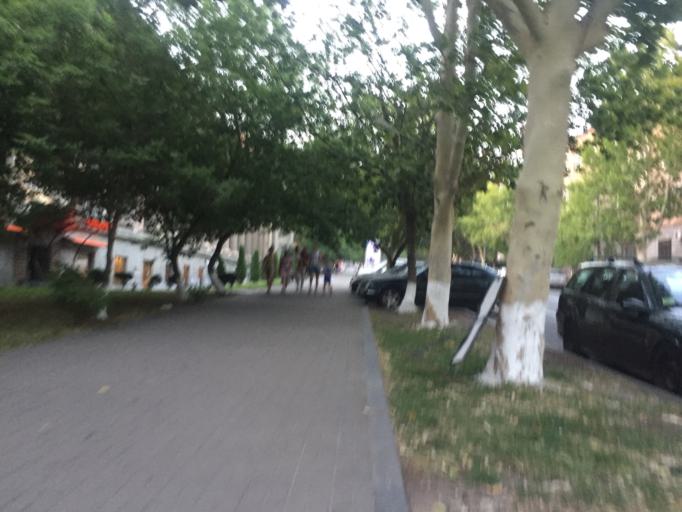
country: AM
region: Yerevan
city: Yerevan
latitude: 40.1885
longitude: 44.5212
